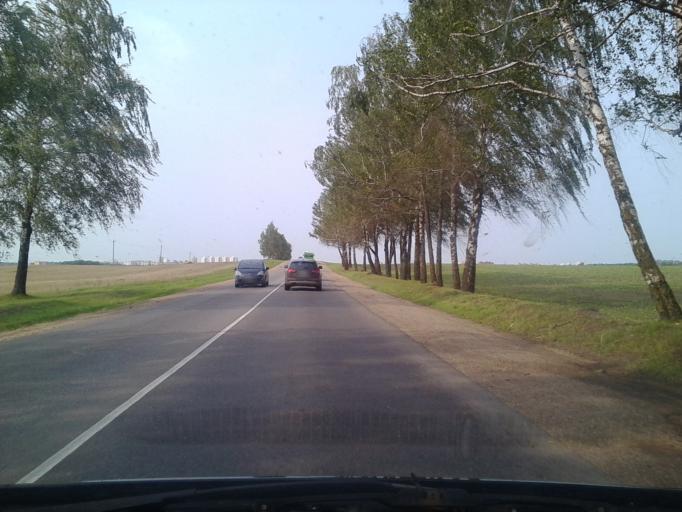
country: BY
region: Minsk
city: Hatava
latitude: 53.8231
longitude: 27.6309
